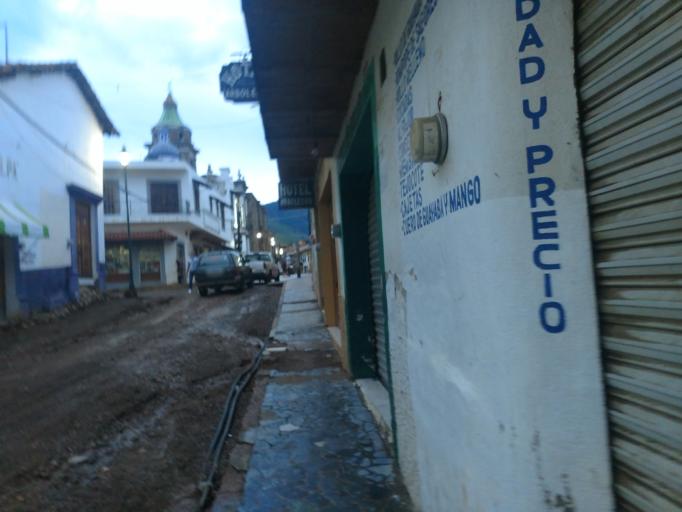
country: MX
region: Jalisco
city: Talpa de Allende
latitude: 20.3799
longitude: -104.8233
